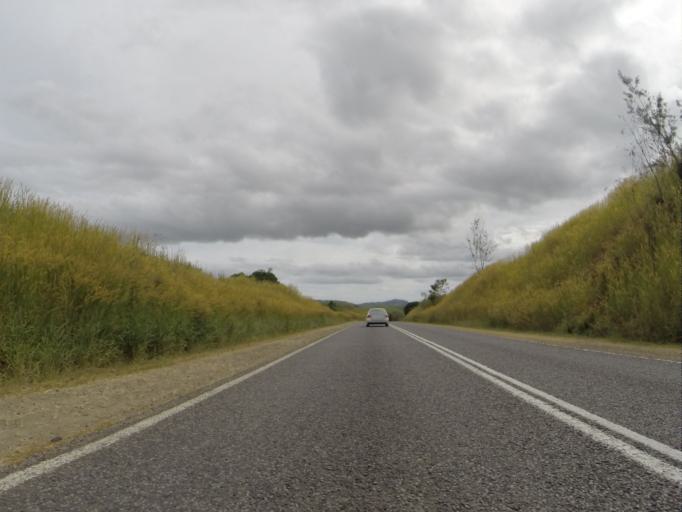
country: FJ
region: Western
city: Nadi
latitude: -18.0309
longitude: 177.3321
